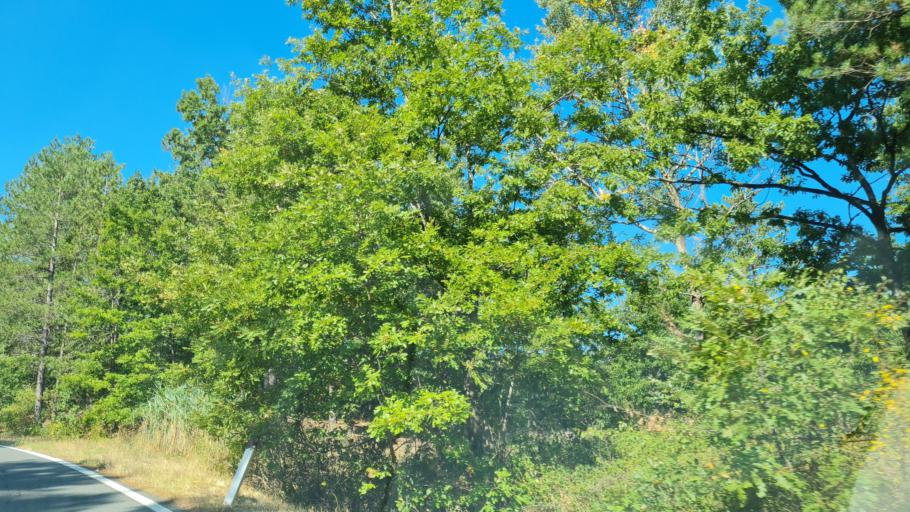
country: IT
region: Tuscany
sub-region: Provincia di Siena
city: Abbadia San Salvatore
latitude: 42.9125
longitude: 11.6839
